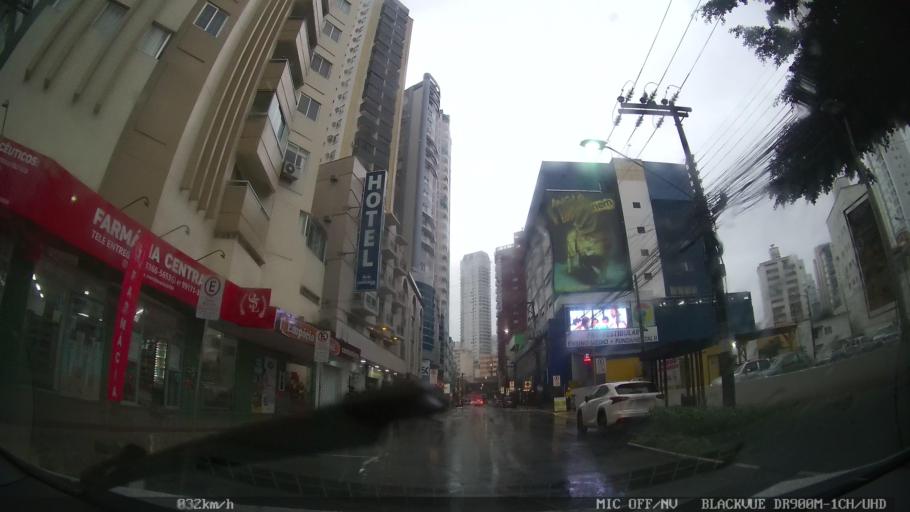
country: BR
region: Santa Catarina
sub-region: Balneario Camboriu
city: Balneario Camboriu
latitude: -26.9884
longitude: -48.6358
